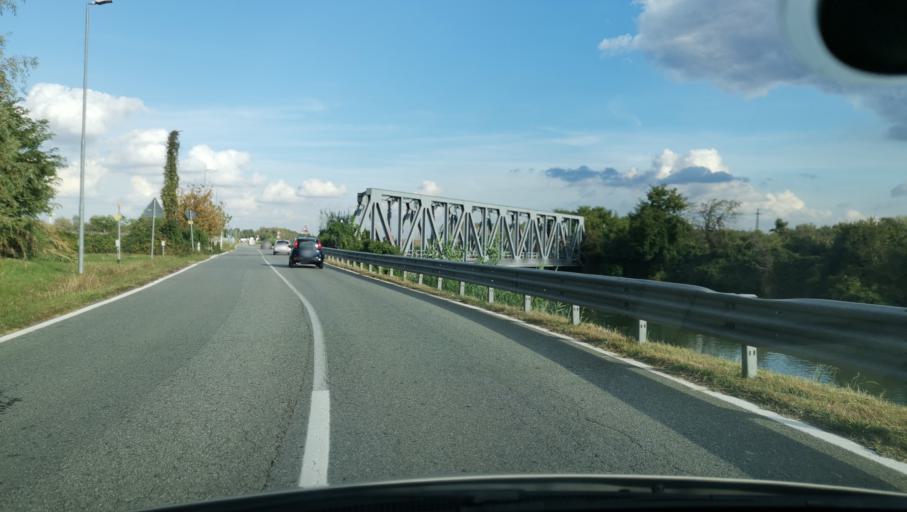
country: IT
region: Piedmont
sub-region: Provincia di Torino
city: Chivasso
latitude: 45.1914
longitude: 7.9076
